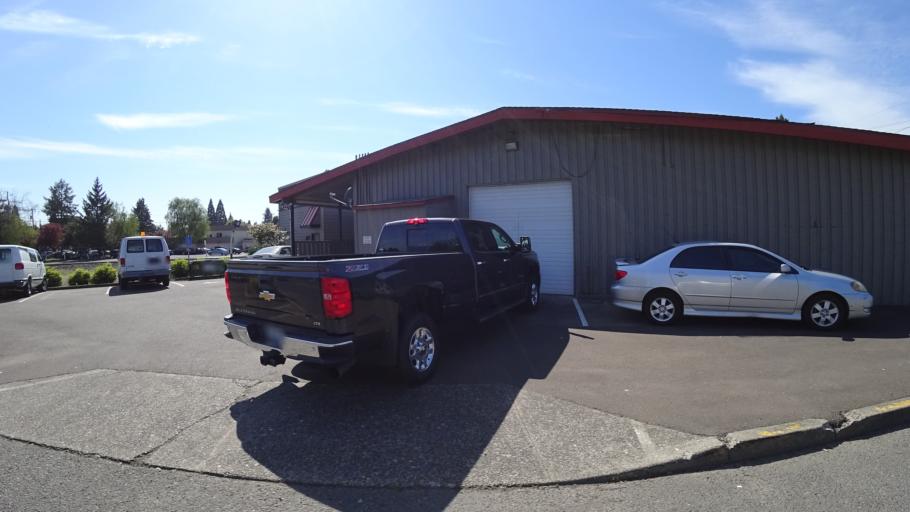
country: US
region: Oregon
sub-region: Clackamas County
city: Milwaukie
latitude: 45.4463
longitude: -122.6297
